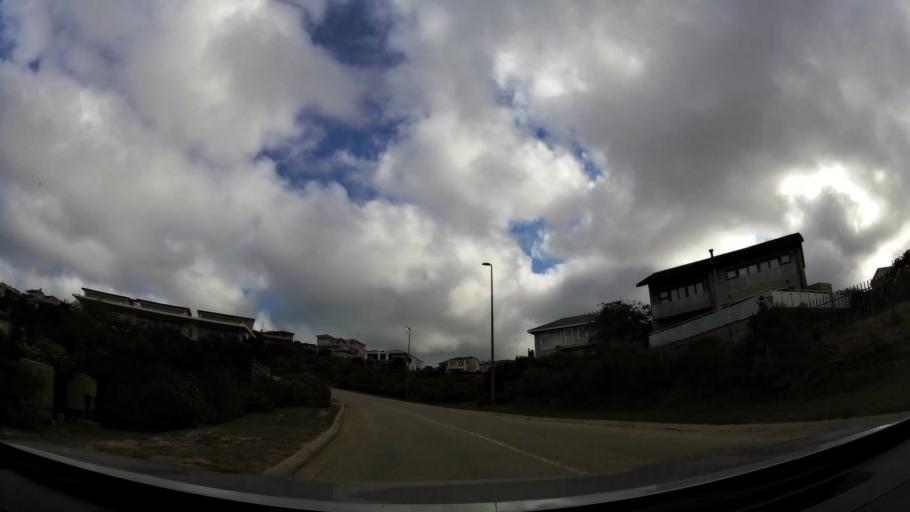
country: ZA
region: Western Cape
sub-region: Eden District Municipality
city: Plettenberg Bay
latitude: -34.0855
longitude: 23.3562
